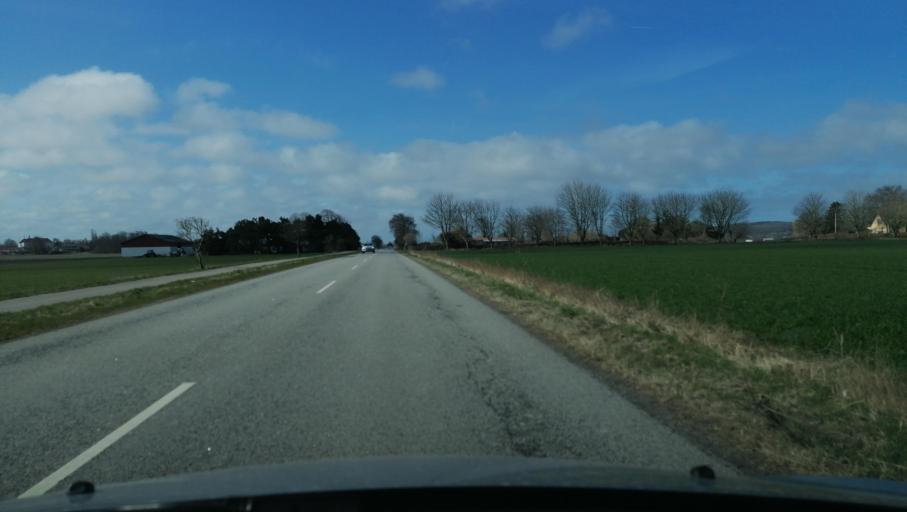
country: DK
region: Zealand
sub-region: Odsherred Kommune
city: Asnaes
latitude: 55.7984
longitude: 11.4702
